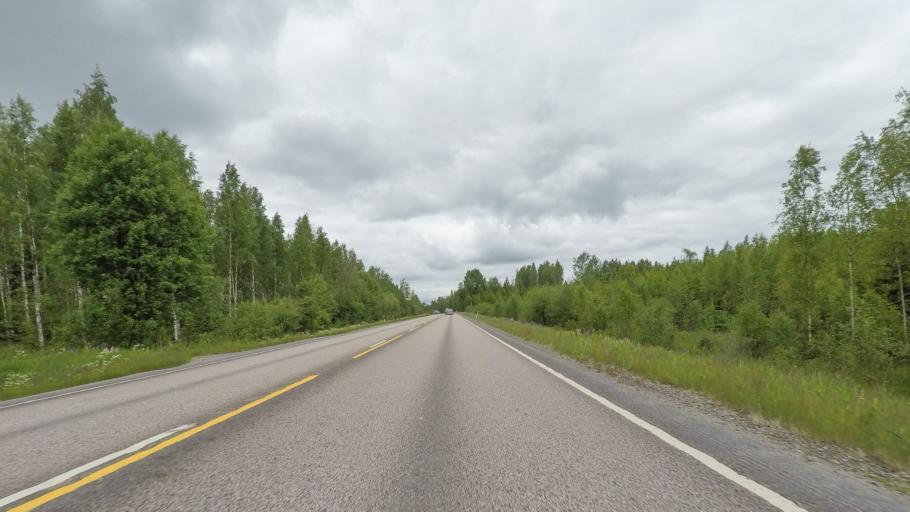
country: FI
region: Central Finland
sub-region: Joutsa
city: Leivonmaeki
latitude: 61.8498
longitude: 26.1007
